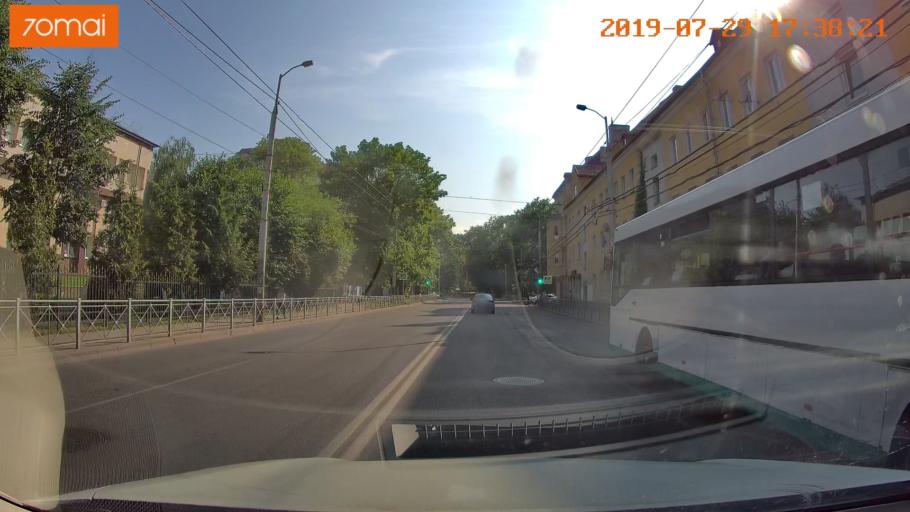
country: RU
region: Kaliningrad
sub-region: Gorod Kaliningrad
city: Kaliningrad
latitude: 54.7237
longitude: 20.5087
